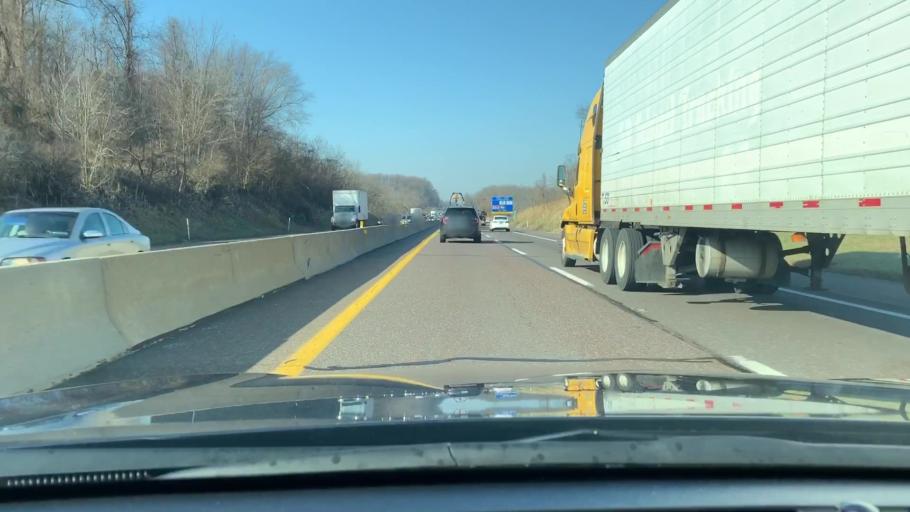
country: US
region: Pennsylvania
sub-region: Chester County
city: Elverson
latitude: 40.1171
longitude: -75.7667
